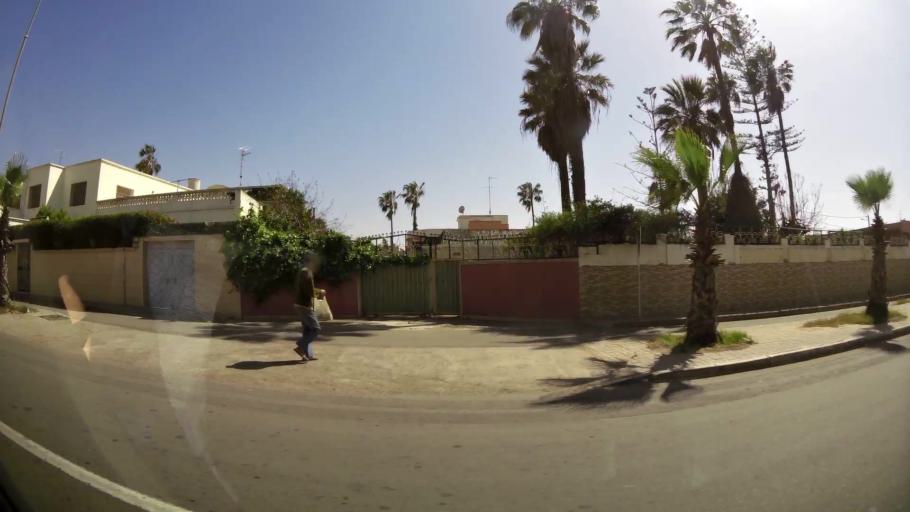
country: MA
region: Souss-Massa-Draa
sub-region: Inezgane-Ait Mellou
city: Inezgane
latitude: 30.3642
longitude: -9.5391
